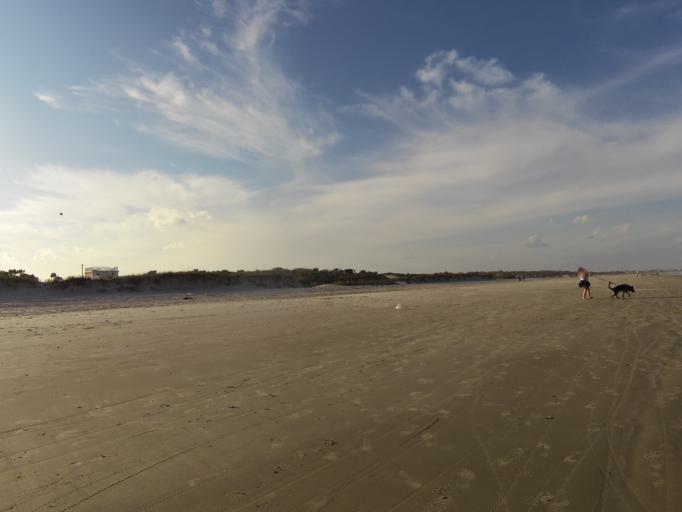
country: US
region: Florida
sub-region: Duval County
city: Atlantic Beach
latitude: 30.3692
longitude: -81.3972
